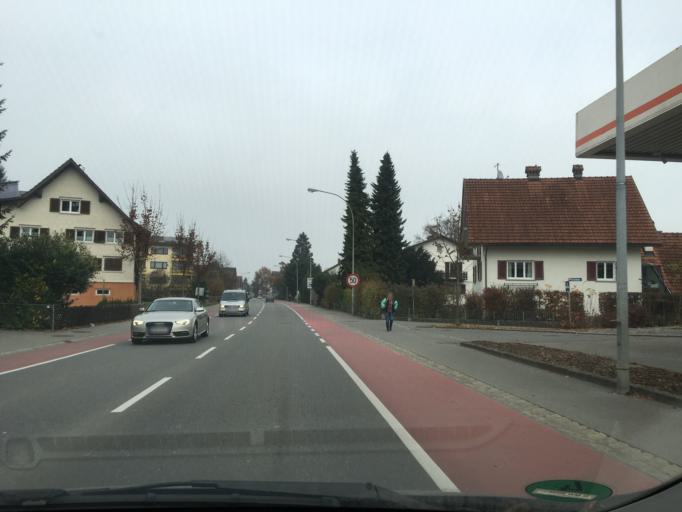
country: AT
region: Vorarlberg
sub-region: Politischer Bezirk Feldkirch
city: Altach
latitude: 47.3531
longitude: 9.6613
